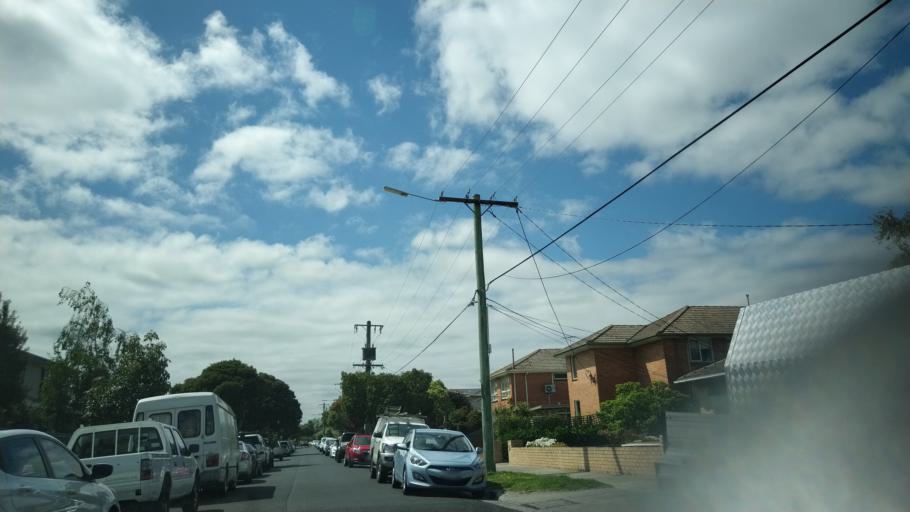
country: AU
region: Victoria
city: Murrumbeena
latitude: -37.8992
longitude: 145.0612
